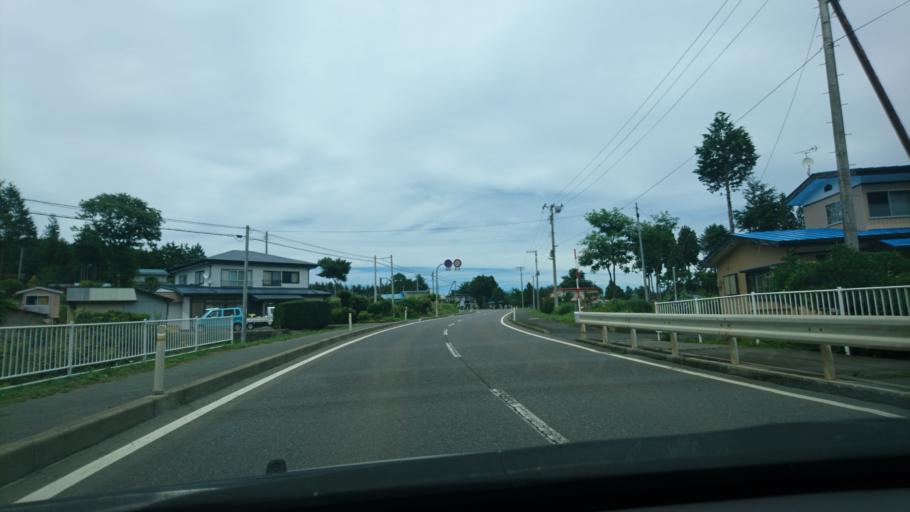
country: JP
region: Iwate
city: Miyako
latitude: 39.9181
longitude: 141.9025
